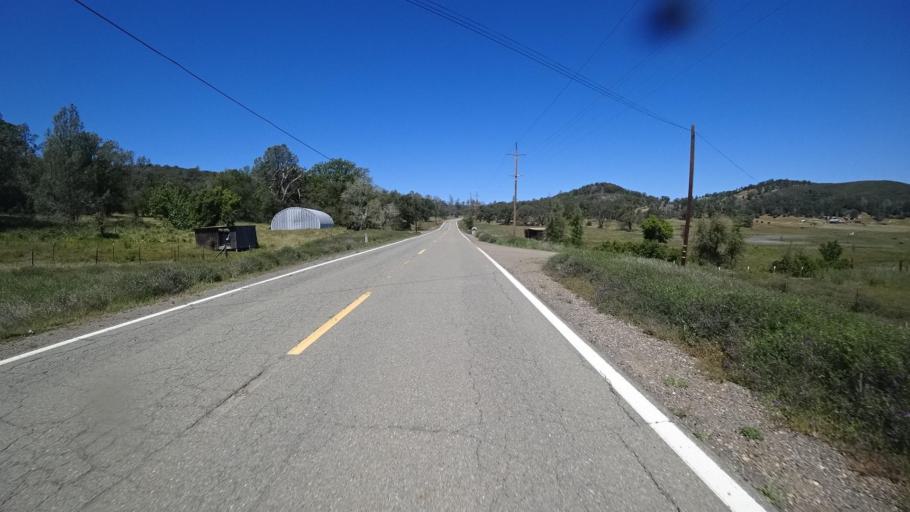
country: US
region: California
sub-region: Lake County
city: Hidden Valley Lake
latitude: 38.8862
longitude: -122.4758
